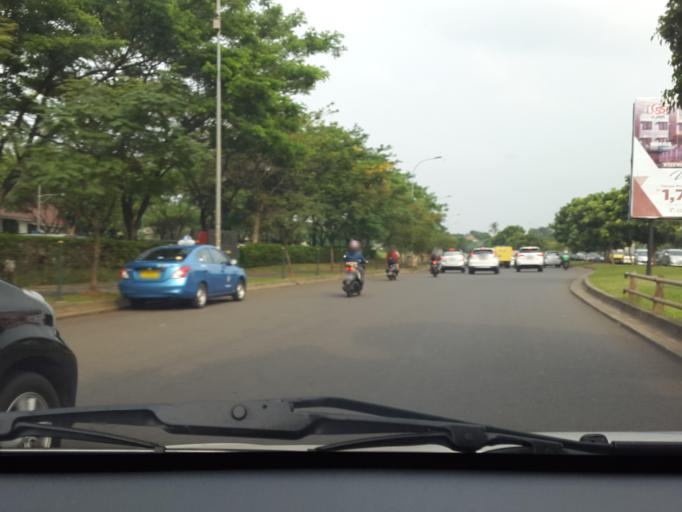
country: ID
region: Banten
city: South Tangerang
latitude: -6.2728
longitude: 106.6993
